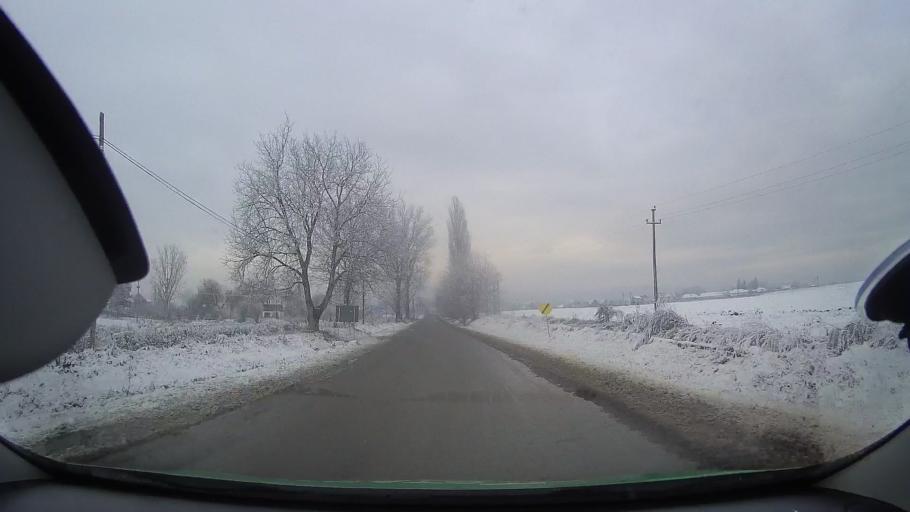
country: RO
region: Mures
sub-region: Comuna Bogata
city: Bogata
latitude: 46.4569
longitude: 24.0813
